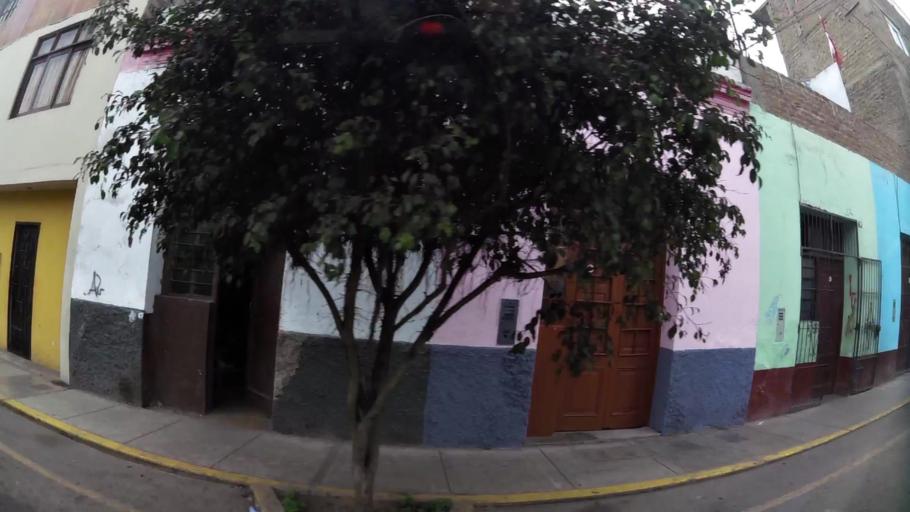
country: PE
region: Lima
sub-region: Lima
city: Surco
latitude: -12.1453
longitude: -77.0169
